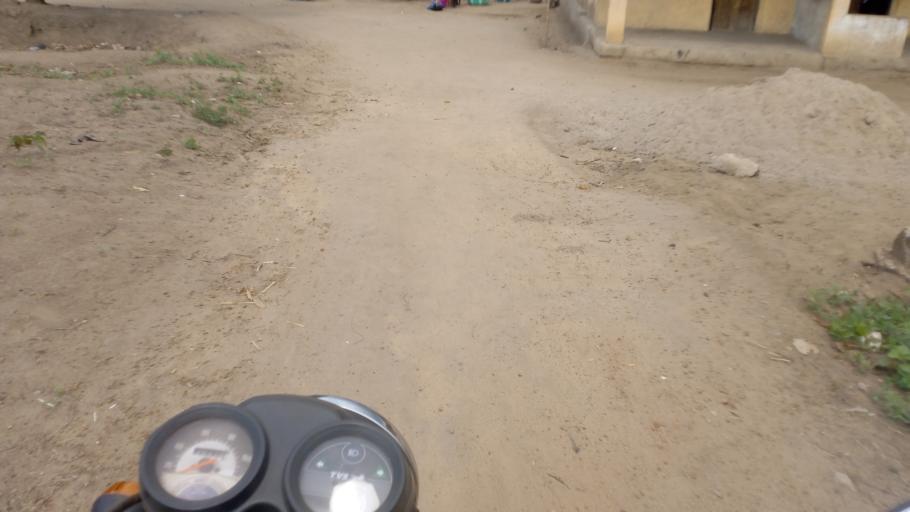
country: SL
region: Western Area
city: Waterloo
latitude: 8.3110
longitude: -13.0617
